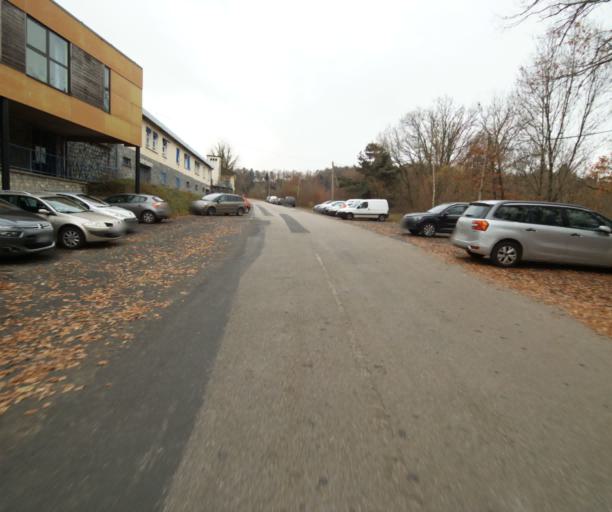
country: FR
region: Limousin
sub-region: Departement de la Correze
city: Tulle
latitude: 45.2710
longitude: 1.7359
